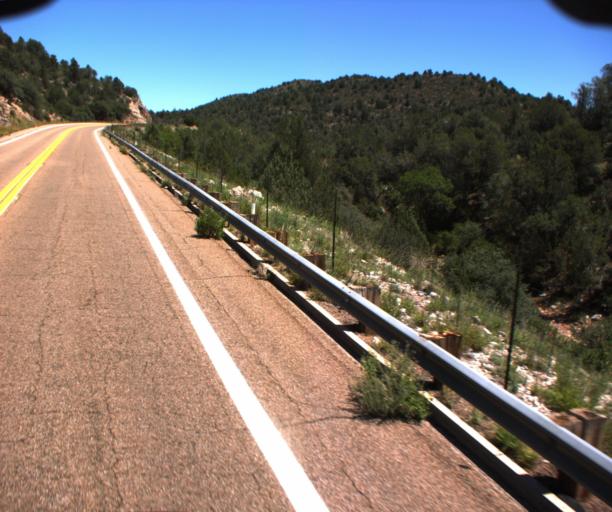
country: US
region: Arizona
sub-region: Navajo County
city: Cibecue
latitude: 33.8464
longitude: -110.4248
